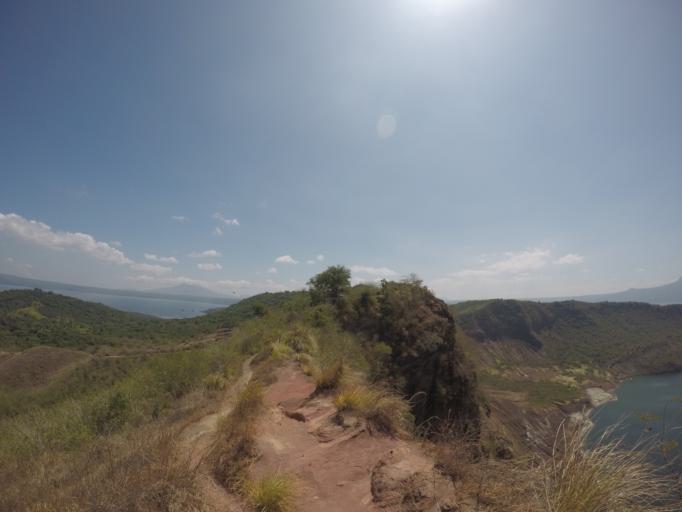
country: PH
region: Calabarzon
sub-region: Province of Batangas
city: Bugaan
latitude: 14.0181
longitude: 120.9980
